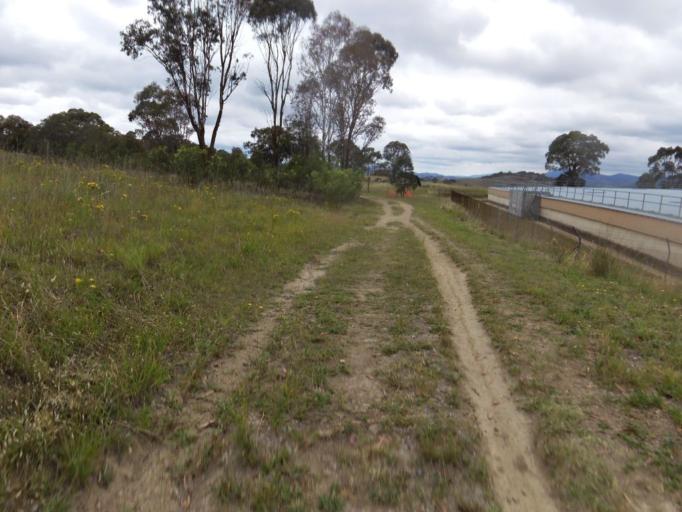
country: AU
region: Australian Capital Territory
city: Forrest
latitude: -35.3600
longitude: 149.0314
